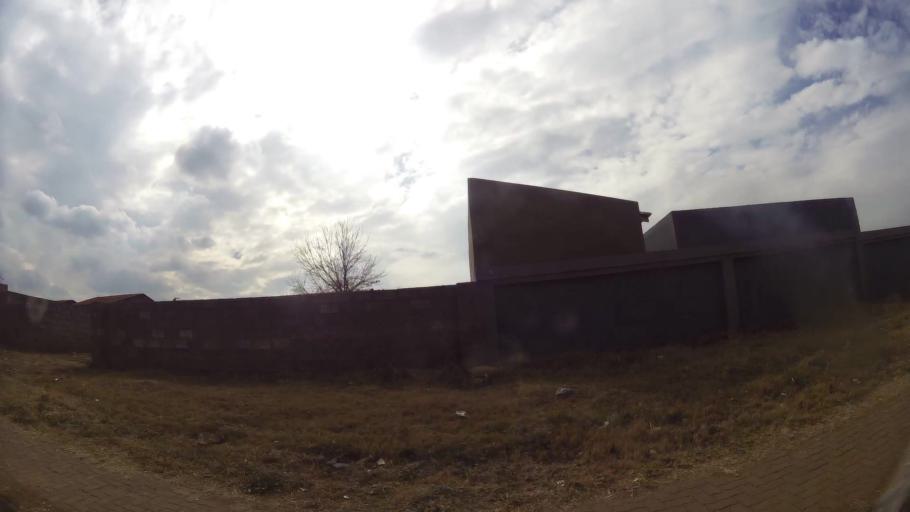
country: ZA
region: Gauteng
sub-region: Ekurhuleni Metropolitan Municipality
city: Germiston
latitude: -26.4082
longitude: 28.1635
